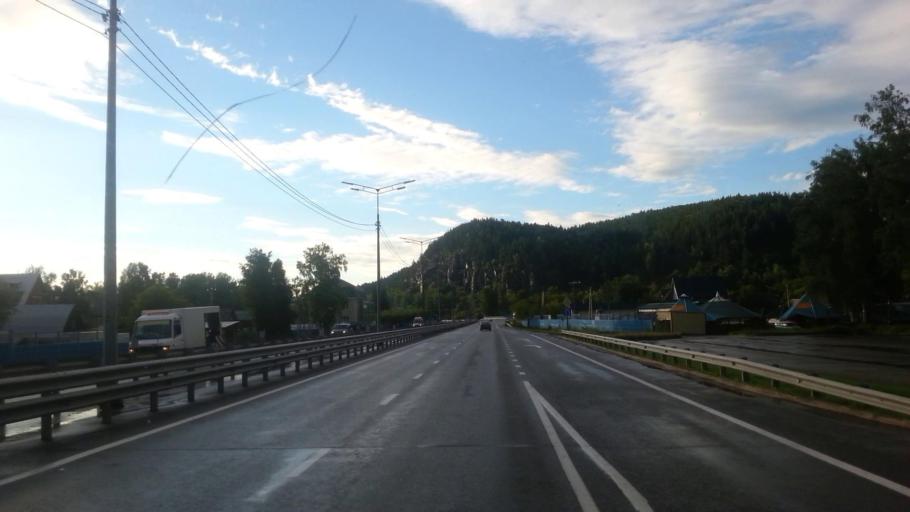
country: RU
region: Altay
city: Souzga
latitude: 51.9149
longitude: 85.8623
